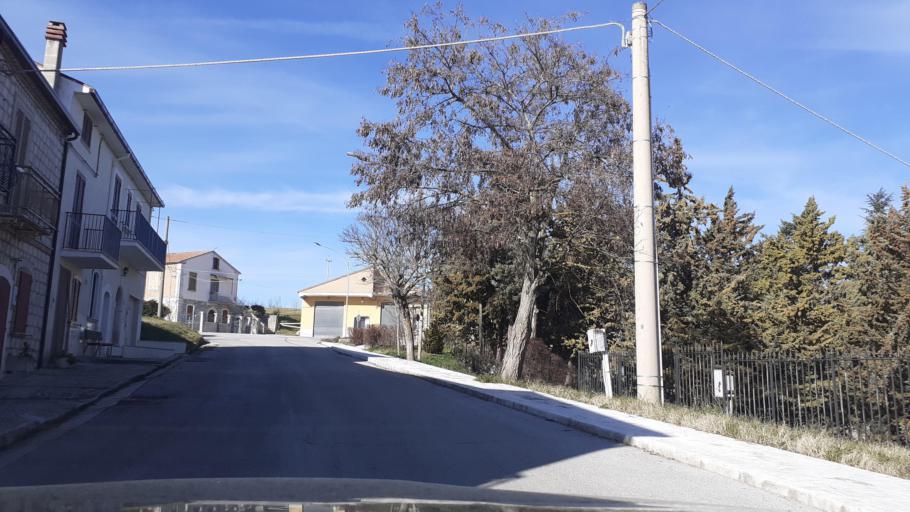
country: IT
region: Molise
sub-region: Provincia di Campobasso
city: Pietracupa
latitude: 41.6822
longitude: 14.5174
